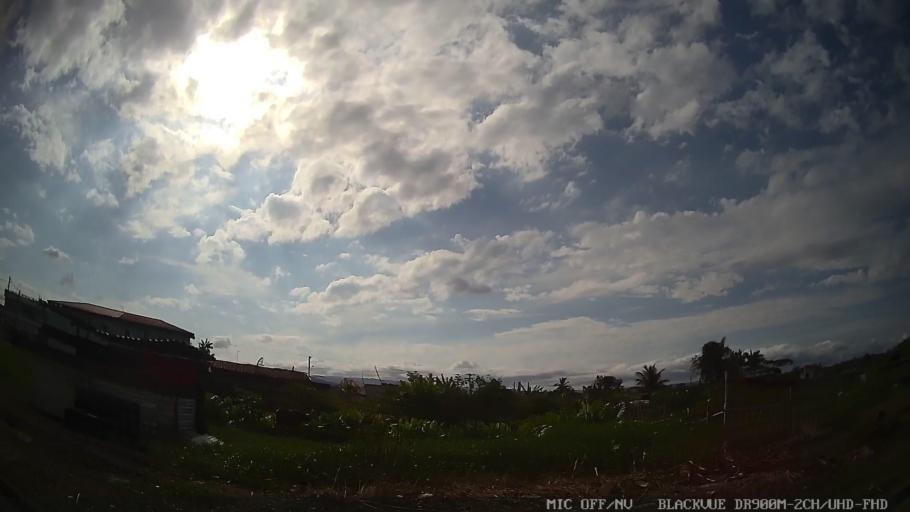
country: BR
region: Sao Paulo
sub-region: Itanhaem
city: Itanhaem
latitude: -24.1783
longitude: -46.8153
